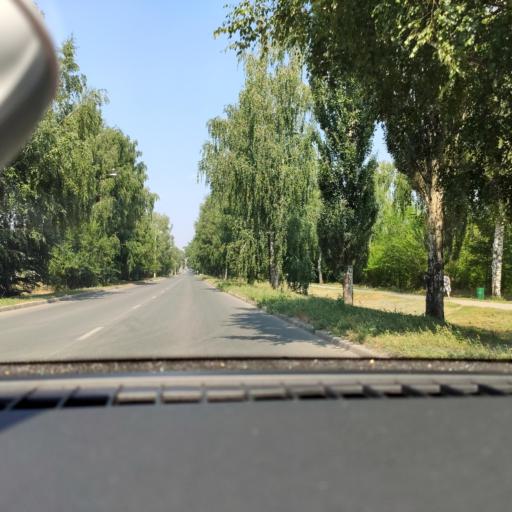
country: RU
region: Samara
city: Bereza
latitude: 53.5130
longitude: 50.1431
